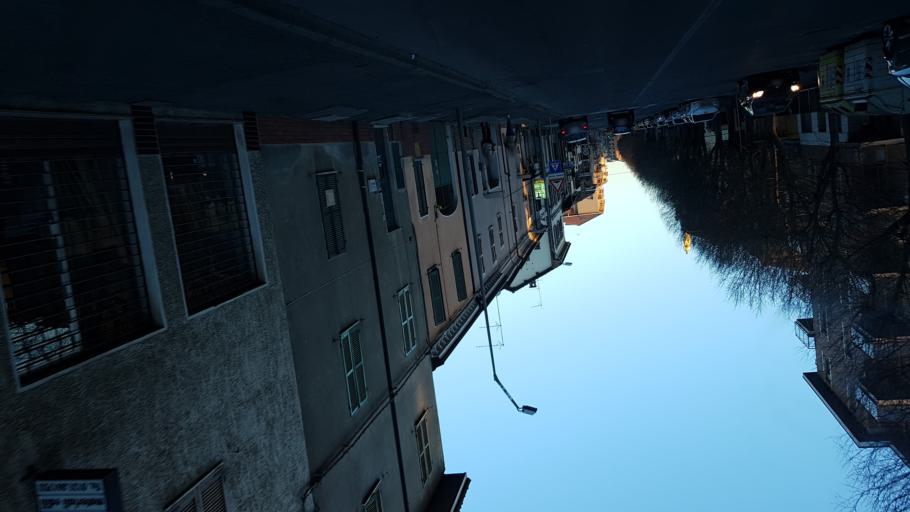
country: IT
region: Piedmont
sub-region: Provincia di Alessandria
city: Tortona
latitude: 44.8843
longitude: 8.8589
